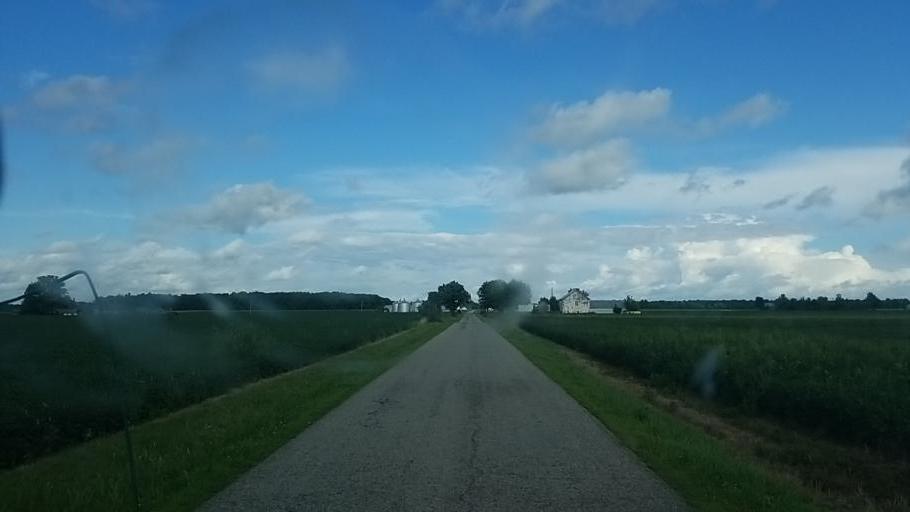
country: US
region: Ohio
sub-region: Hardin County
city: Forest
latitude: 40.7596
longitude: -83.4549
